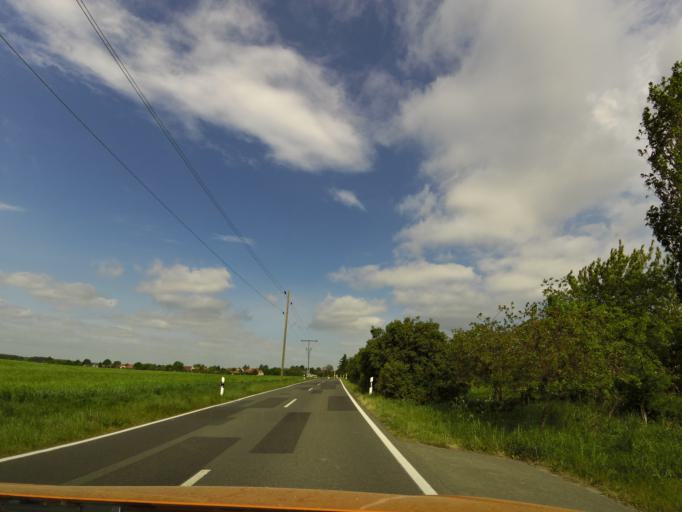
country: DE
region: Brandenburg
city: Belzig
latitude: 52.0988
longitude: 12.5647
